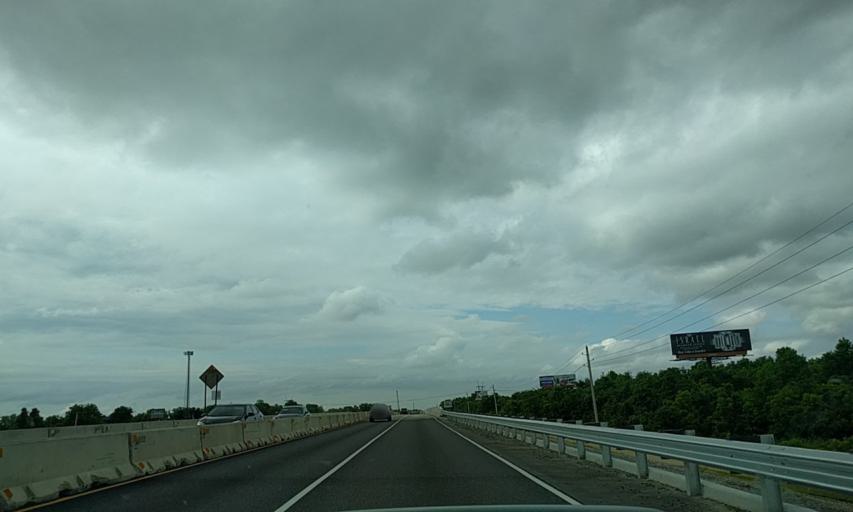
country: US
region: Oklahoma
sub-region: Tulsa County
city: Owasso
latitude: 36.2492
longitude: -95.8483
